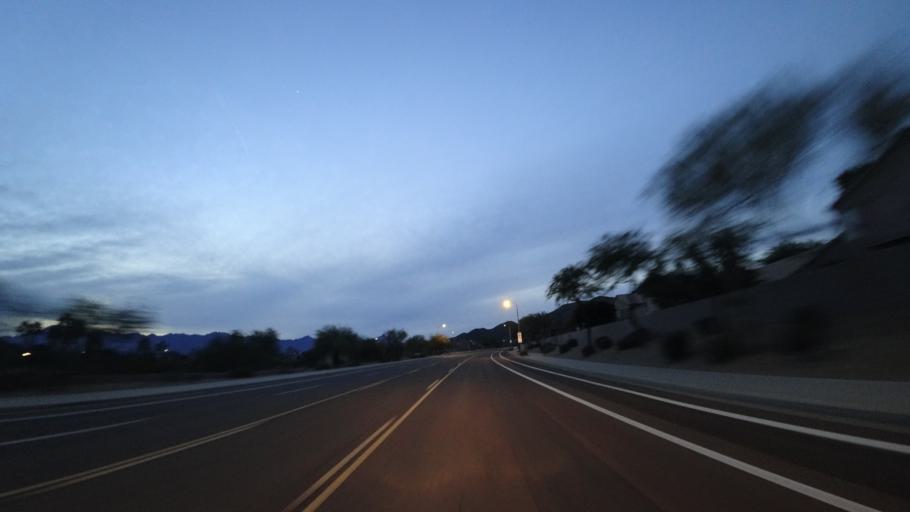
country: US
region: Arizona
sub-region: Maricopa County
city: Laveen
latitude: 33.3023
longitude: -112.0930
